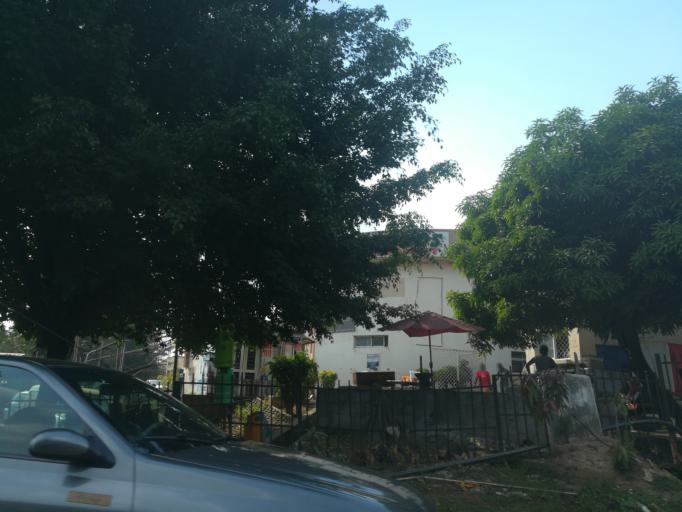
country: NG
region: Abuja Federal Capital Territory
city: Abuja
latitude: 9.0795
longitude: 7.4169
